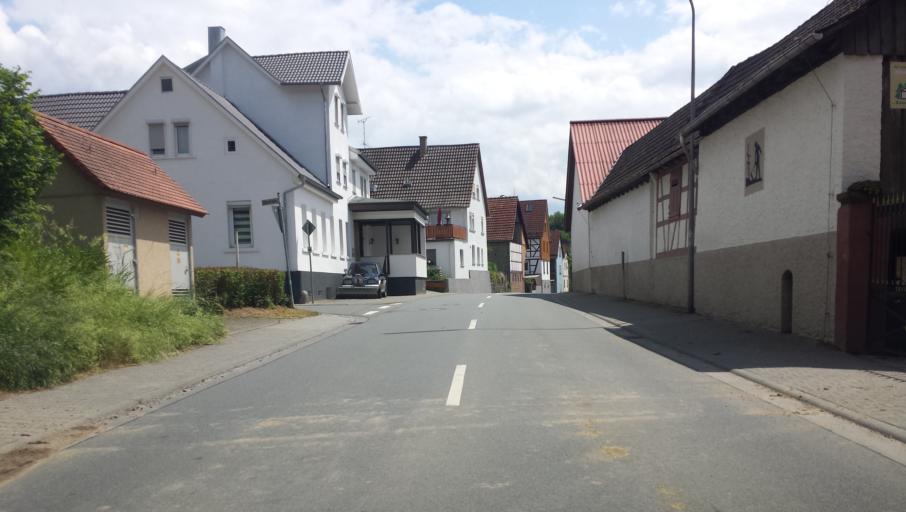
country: DE
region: Hesse
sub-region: Regierungsbezirk Darmstadt
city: Lindenfels
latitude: 49.6674
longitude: 8.7671
